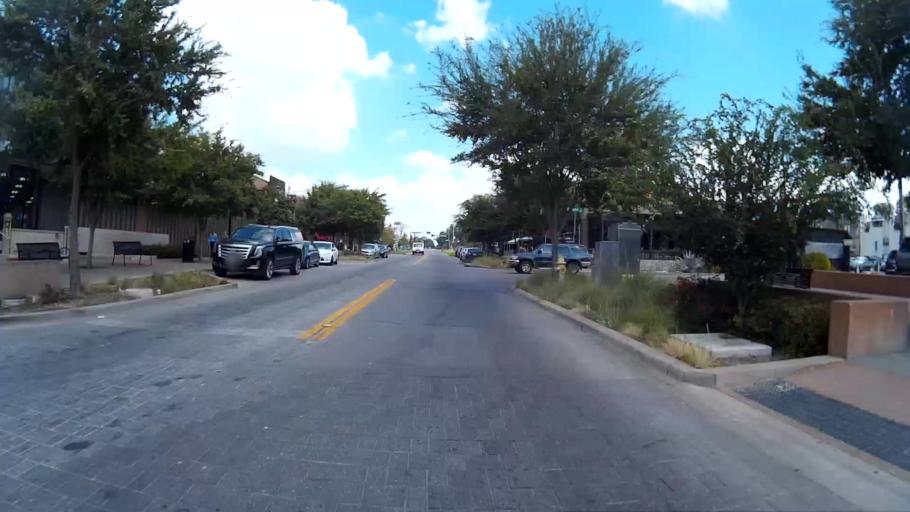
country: US
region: Texas
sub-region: Dallas County
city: Highland Park
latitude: 32.8145
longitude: -96.7702
